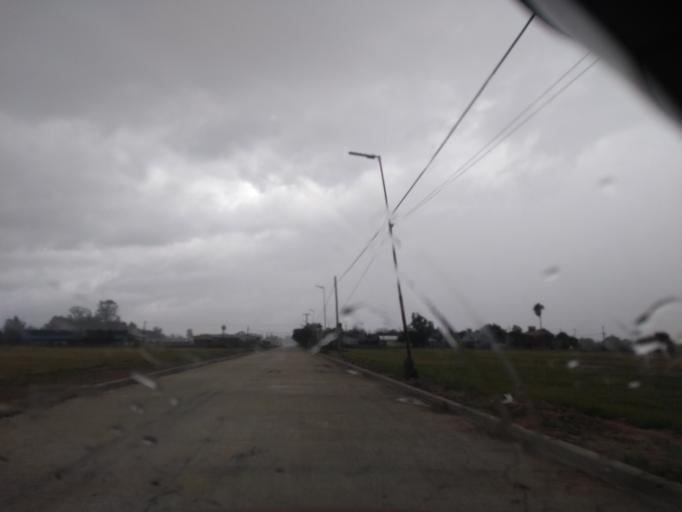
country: AR
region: Chaco
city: Fontana
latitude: -27.4213
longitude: -59.0453
